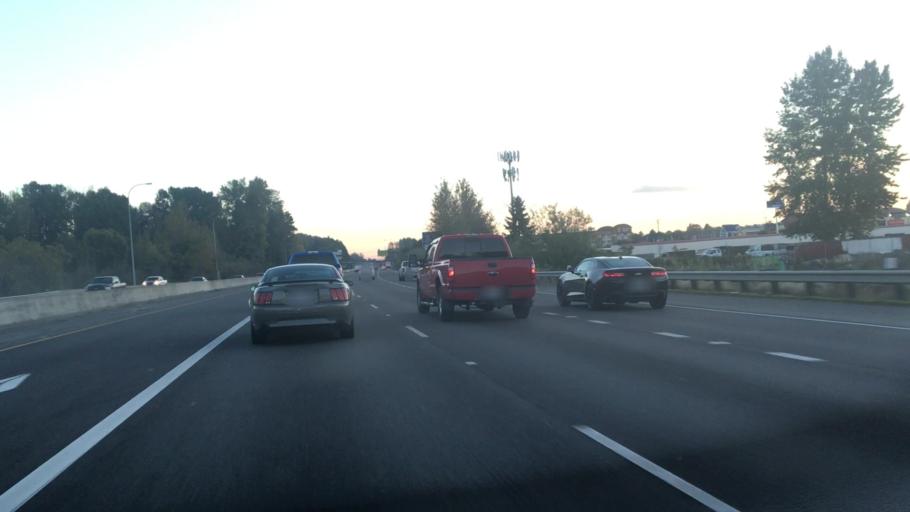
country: US
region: Washington
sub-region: King County
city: Renton
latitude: 47.4497
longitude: -122.2136
